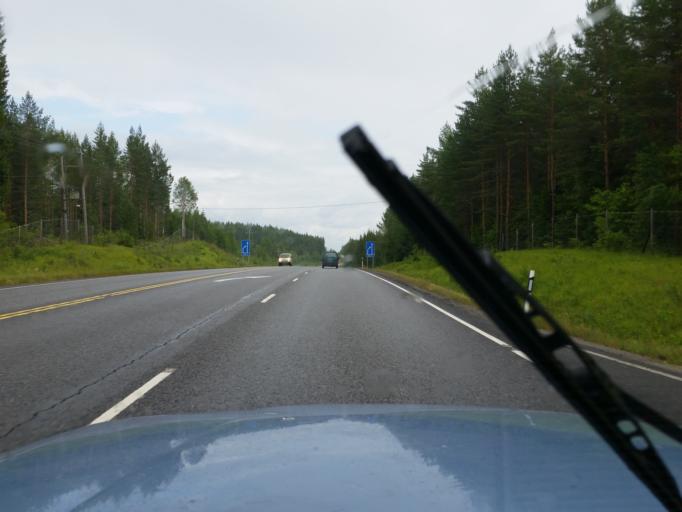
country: FI
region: Southern Savonia
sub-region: Mikkeli
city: Pertunmaa
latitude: 61.4367
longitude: 26.5101
